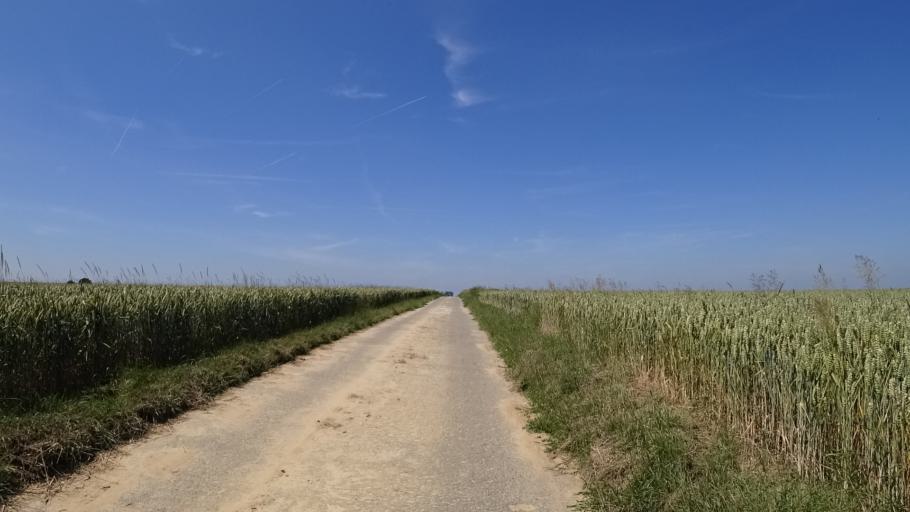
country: BE
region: Wallonia
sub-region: Province du Brabant Wallon
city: Perwez
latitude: 50.6564
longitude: 4.8465
